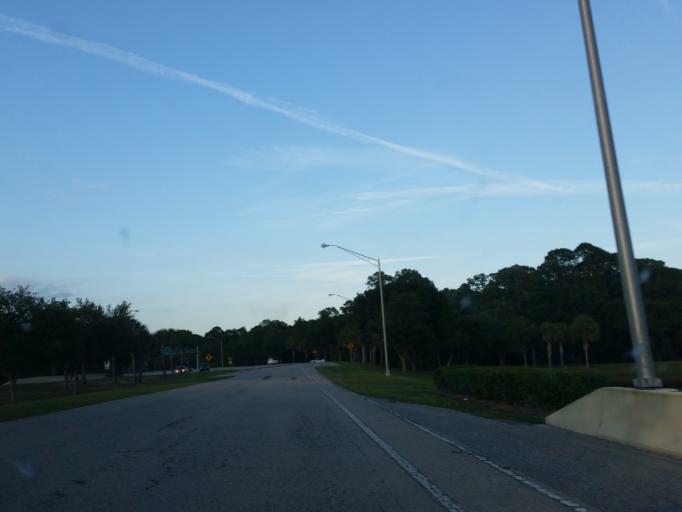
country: US
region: Florida
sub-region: Sarasota County
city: North Port
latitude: 27.0944
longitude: -82.2061
